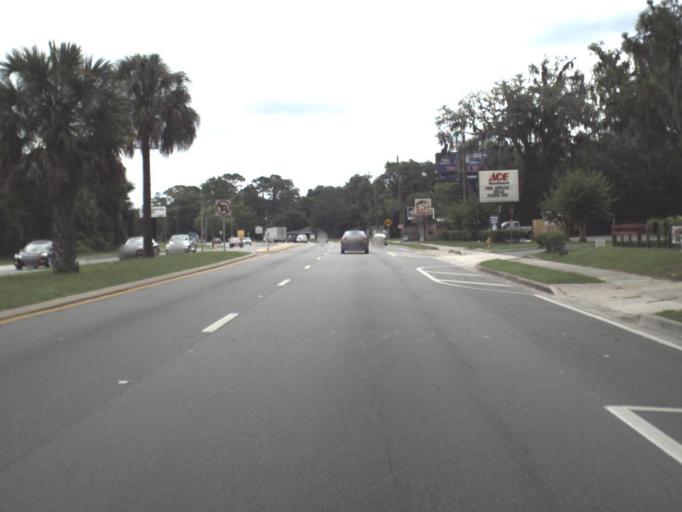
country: US
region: Florida
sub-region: Putnam County
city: East Palatka
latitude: 29.6433
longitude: -81.6103
